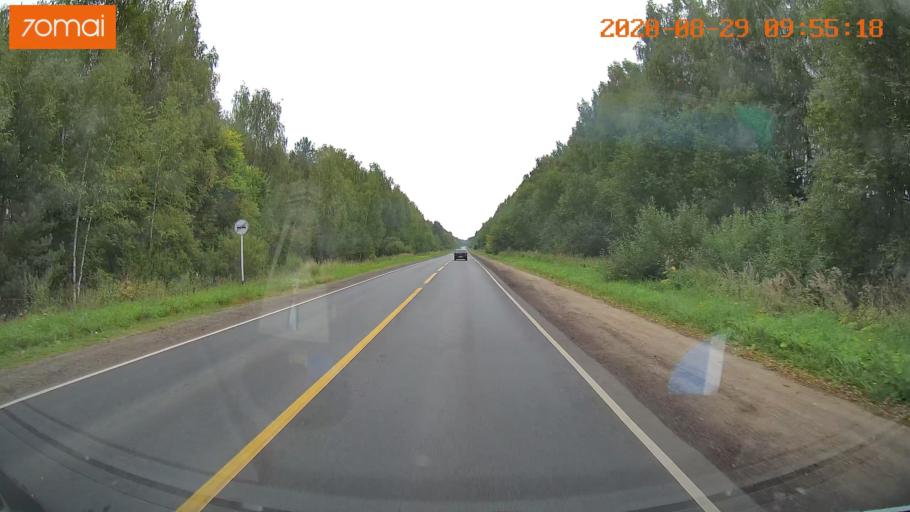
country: RU
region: Ivanovo
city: Zarechnyy
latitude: 57.4225
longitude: 42.2599
